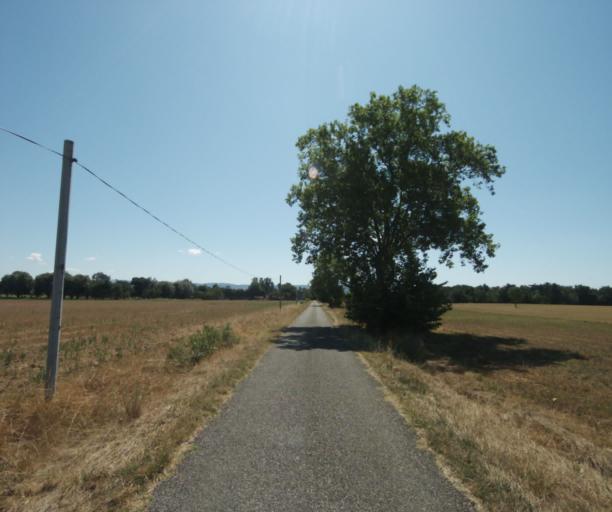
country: FR
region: Midi-Pyrenees
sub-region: Departement de la Haute-Garonne
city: Revel
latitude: 43.4853
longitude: 1.9660
